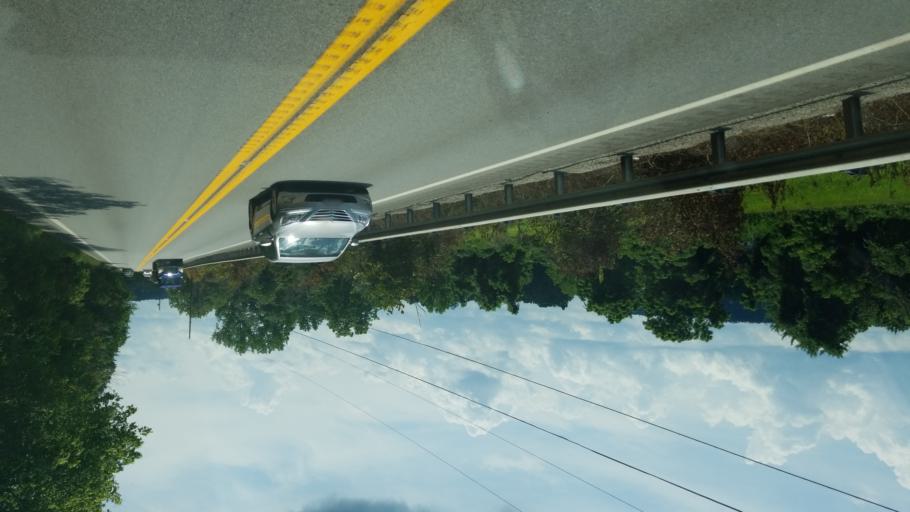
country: US
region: West Virginia
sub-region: Putnam County
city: Buffalo
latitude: 38.6131
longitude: -81.9936
